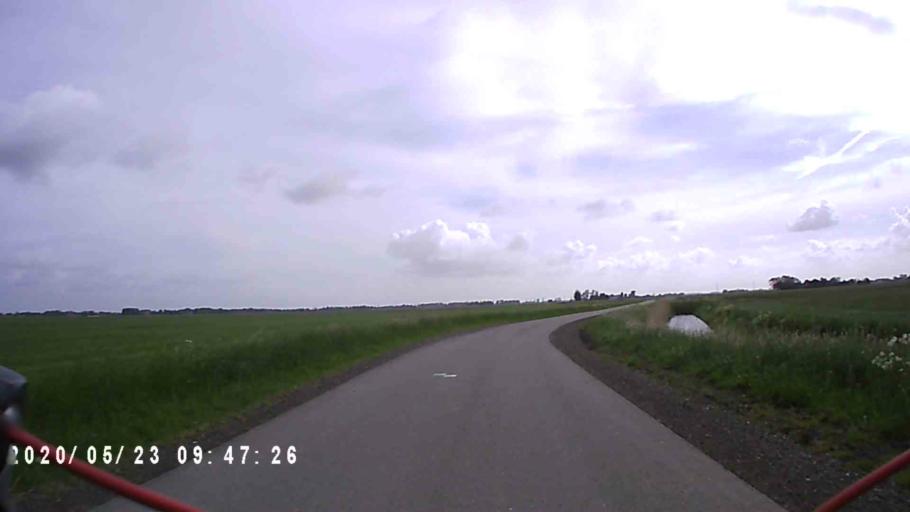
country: NL
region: Groningen
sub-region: Gemeente Slochteren
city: Slochteren
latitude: 53.2898
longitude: 6.7527
